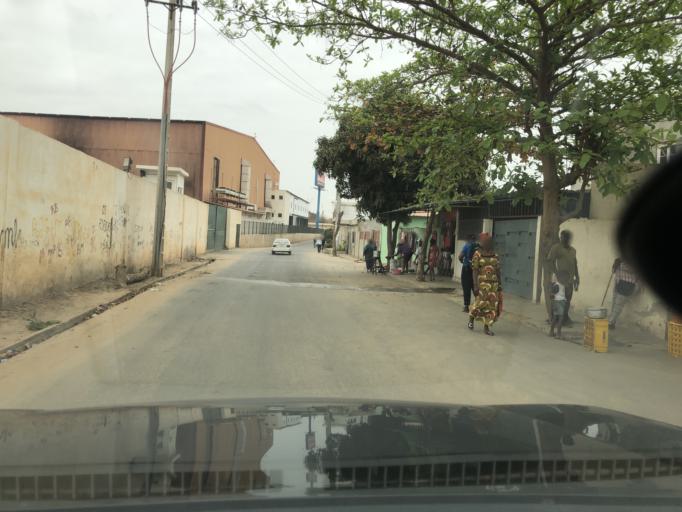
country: AO
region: Luanda
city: Luanda
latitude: -8.8999
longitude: 13.2586
